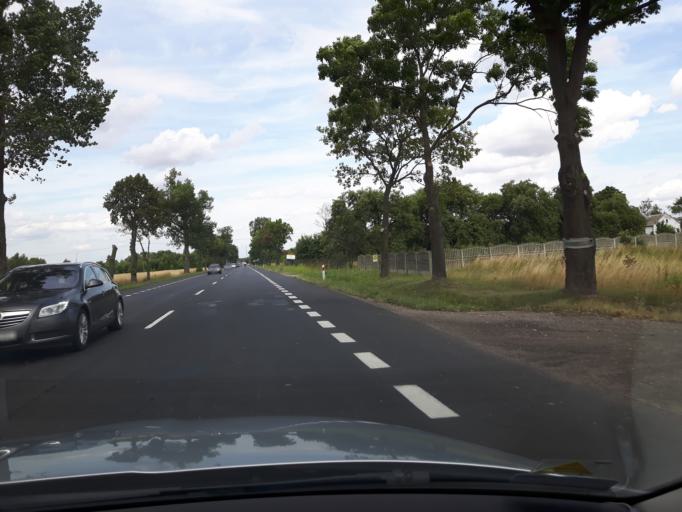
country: PL
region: Masovian Voivodeship
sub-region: Powiat mlawski
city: Wisniewo
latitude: 52.9911
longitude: 20.3247
